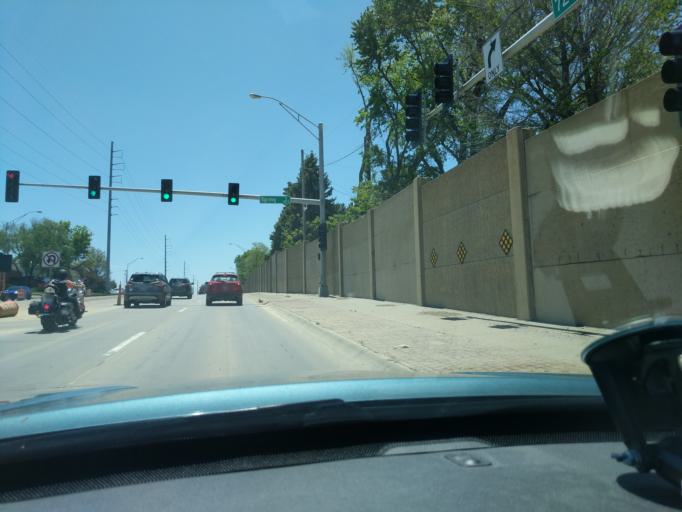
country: US
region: Nebraska
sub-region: Douglas County
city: Ralston
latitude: 41.2308
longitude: -96.0240
